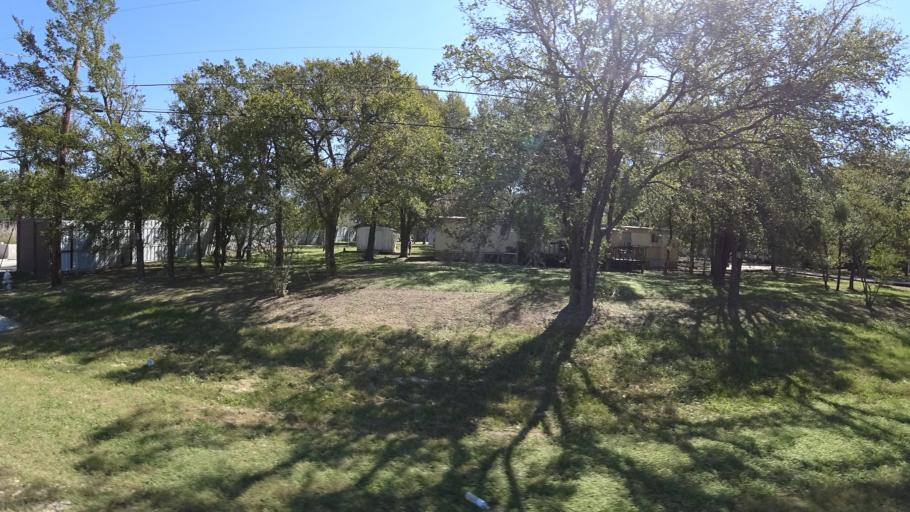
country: US
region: Texas
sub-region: Travis County
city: Hornsby Bend
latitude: 30.2747
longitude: -97.6136
